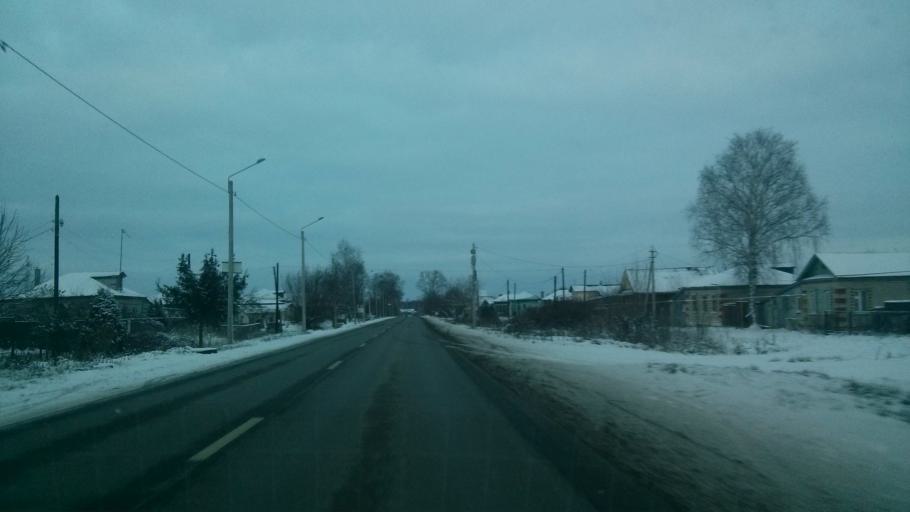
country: RU
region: Nizjnij Novgorod
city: Vorsma
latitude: 56.0325
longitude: 43.3642
